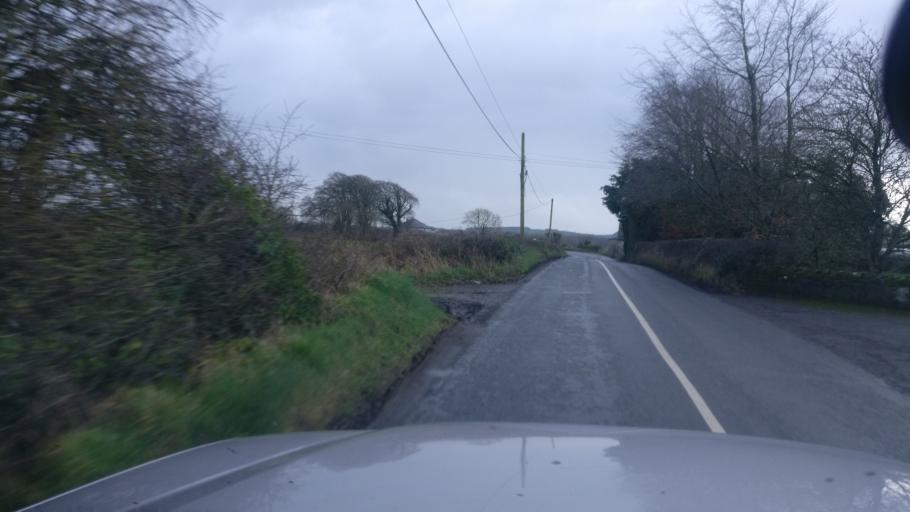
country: IE
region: Munster
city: Nenagh Bridge
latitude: 52.9898
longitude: -8.1179
